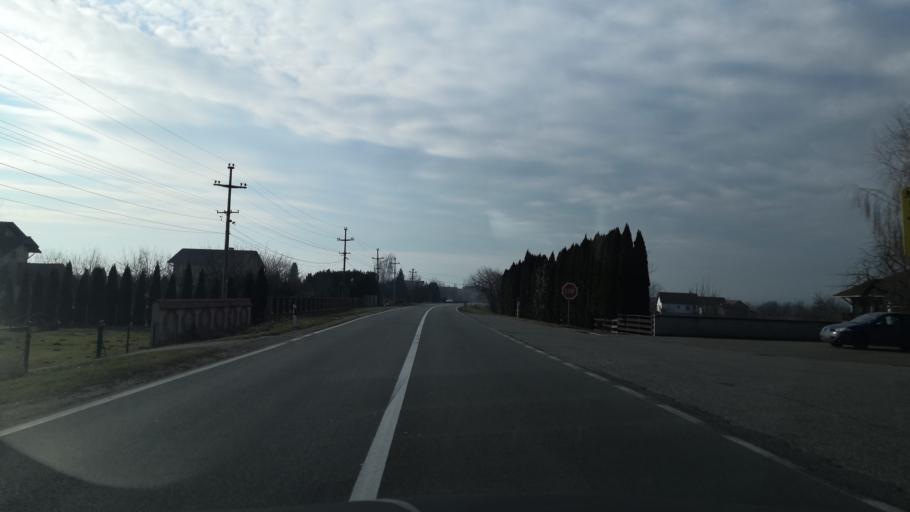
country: RS
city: Lesnica
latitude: 44.6391
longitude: 19.2781
